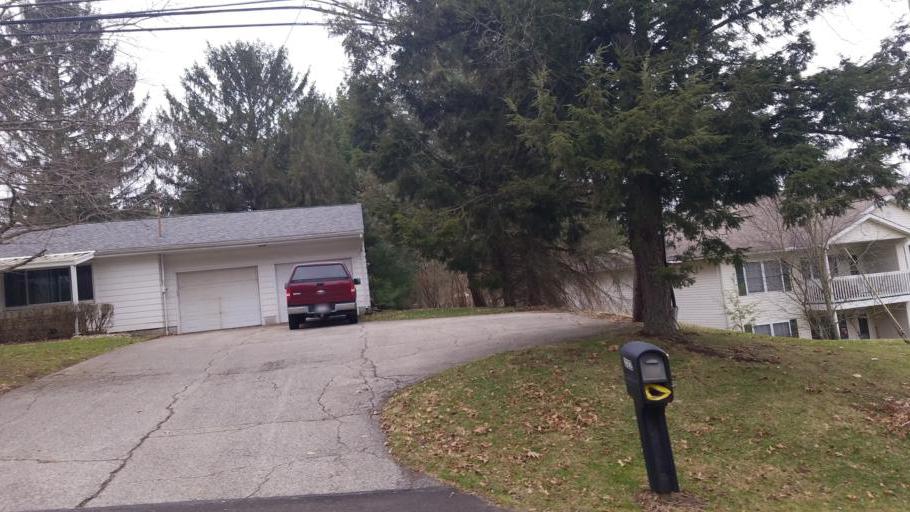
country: US
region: Ohio
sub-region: Sandusky County
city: Bellville
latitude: 40.6147
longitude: -82.5114
